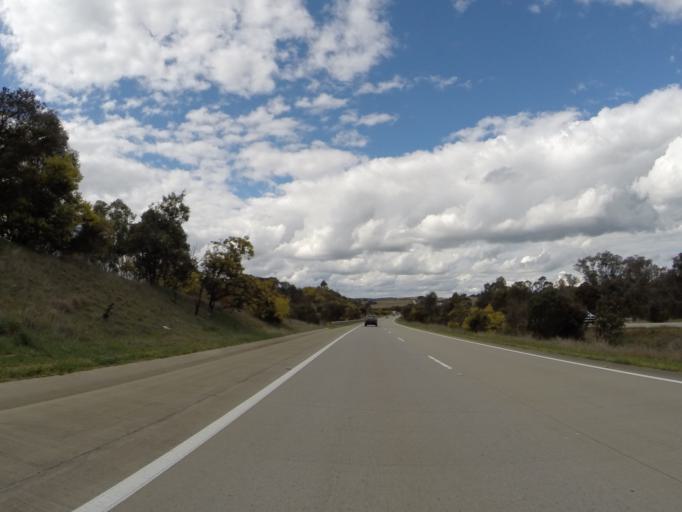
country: AU
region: New South Wales
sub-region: Yass Valley
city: Murrumbateman
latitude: -34.8125
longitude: 149.1135
